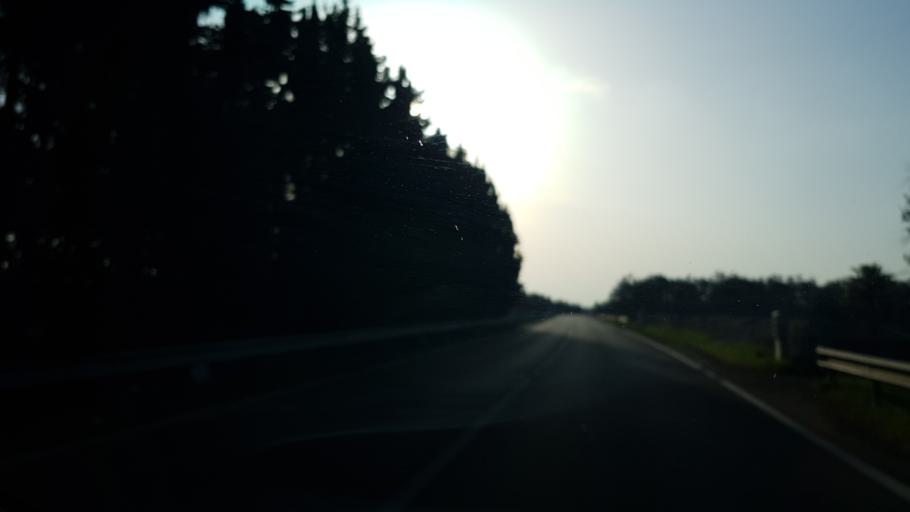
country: IT
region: Apulia
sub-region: Provincia di Lecce
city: Novoli
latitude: 40.3986
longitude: 18.0539
